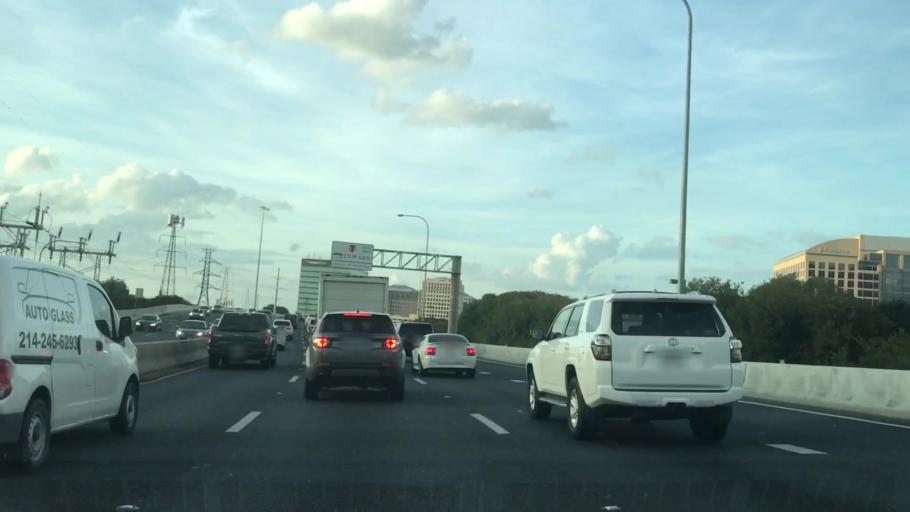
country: US
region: Texas
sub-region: Dallas County
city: Addison
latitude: 32.9305
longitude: -96.8212
